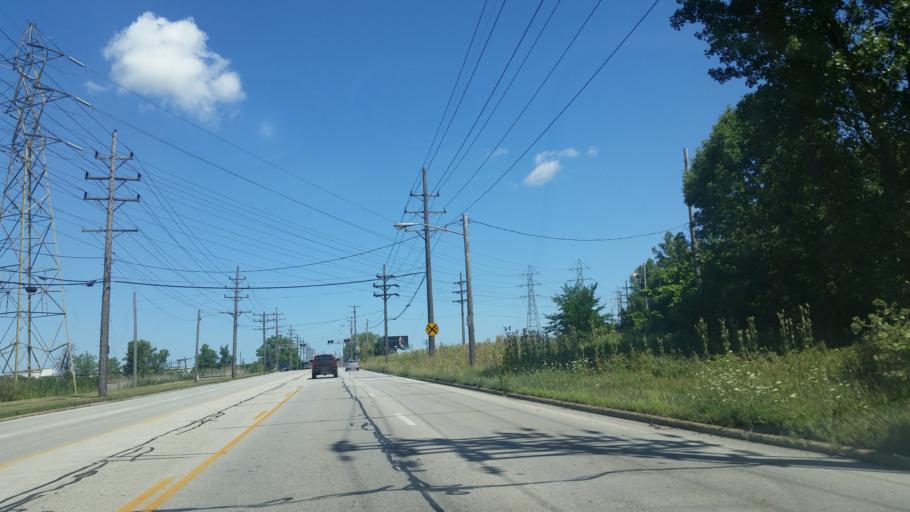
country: US
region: Ohio
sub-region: Cuyahoga County
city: Brook Park
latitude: 41.4092
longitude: -81.7840
